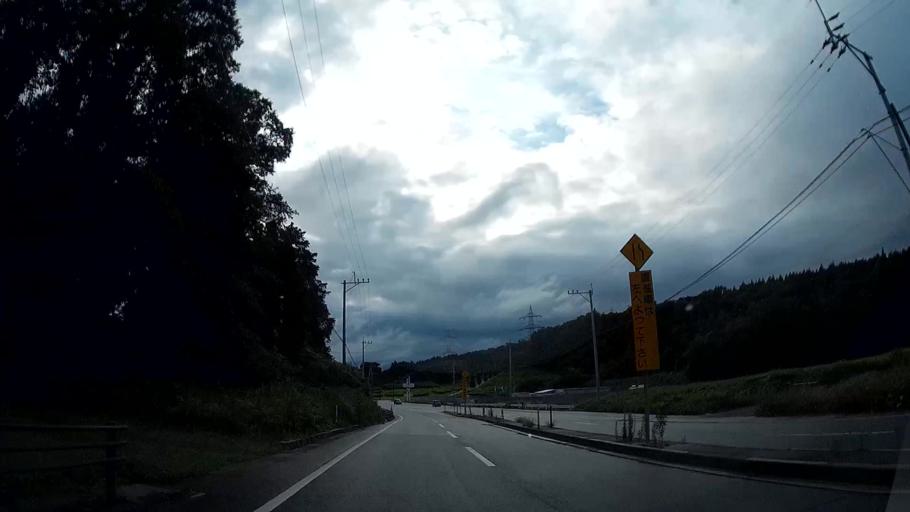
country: JP
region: Kumamoto
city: Ozu
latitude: 32.8754
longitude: 130.9301
